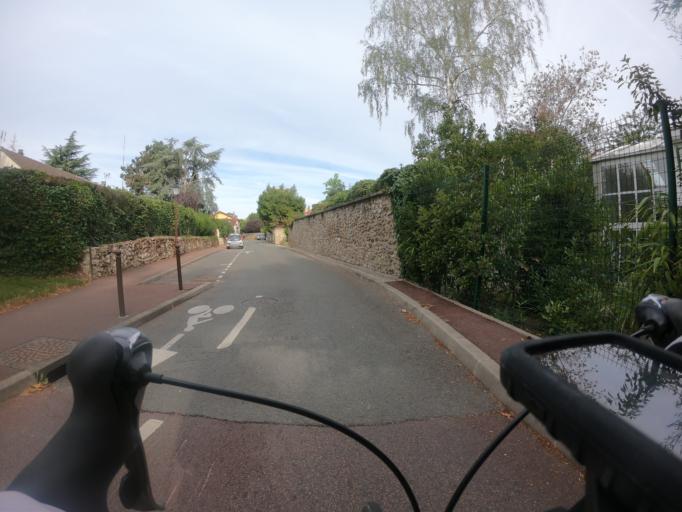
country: FR
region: Ile-de-France
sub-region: Departement des Yvelines
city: Les Loges-en-Josas
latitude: 48.7643
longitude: 2.1451
